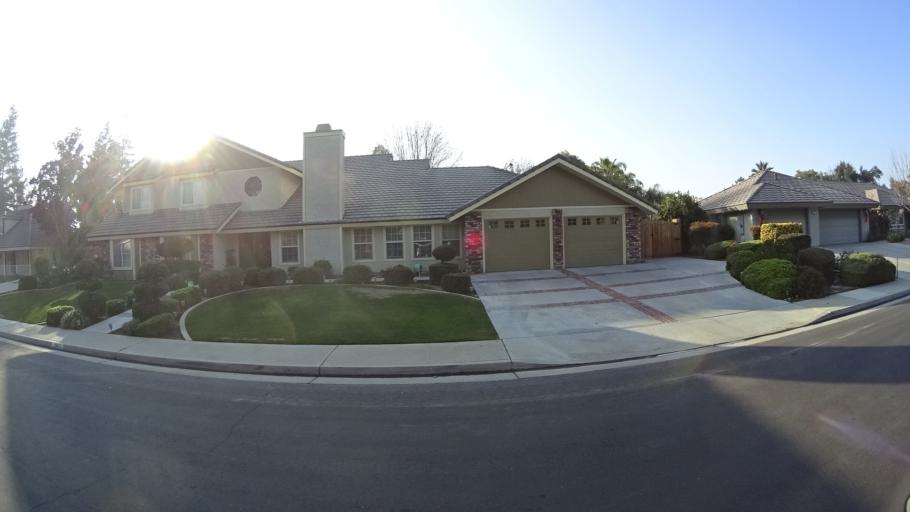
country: US
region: California
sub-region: Kern County
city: Greenacres
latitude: 35.3373
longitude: -119.0998
